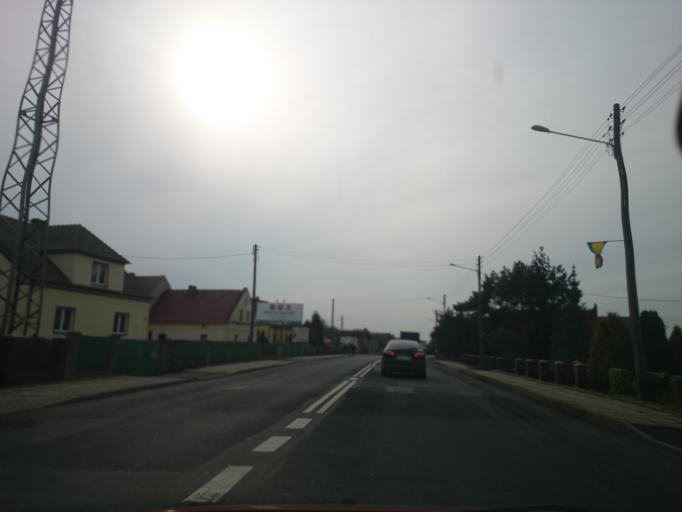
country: PL
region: Opole Voivodeship
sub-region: Powiat opolski
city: Chroscina
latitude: 50.6860
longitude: 17.8156
